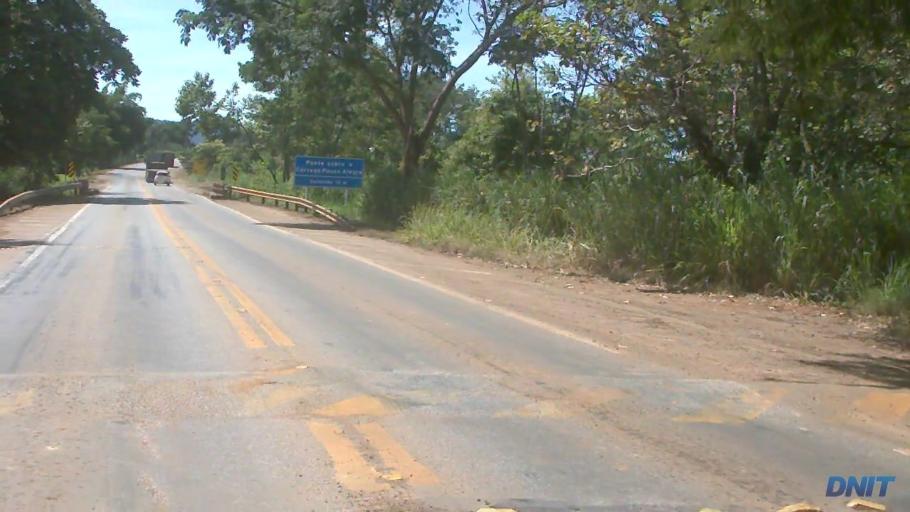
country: BR
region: Goias
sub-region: Barro Alto
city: Barro Alto
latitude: -15.0525
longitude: -48.8838
